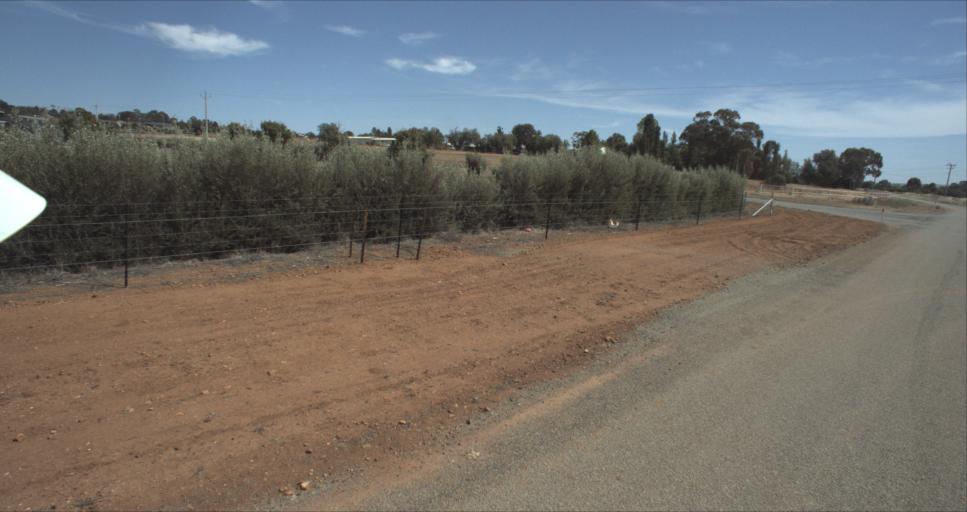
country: AU
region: New South Wales
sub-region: Leeton
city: Leeton
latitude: -34.5782
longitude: 146.4553
